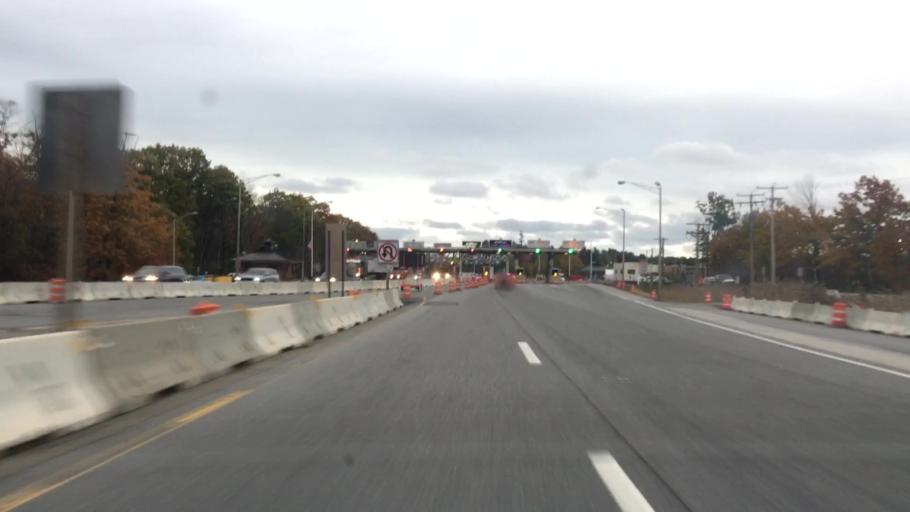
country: US
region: Maine
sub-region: Cumberland County
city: South Portland Gardens
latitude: 43.6258
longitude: -70.3445
